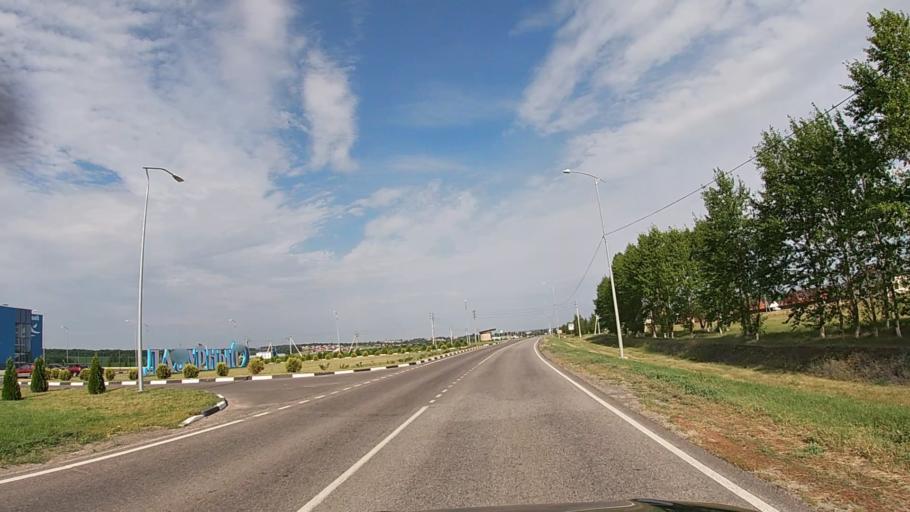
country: RU
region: Belgorod
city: Krasnaya Yaruga
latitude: 50.7964
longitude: 35.6926
